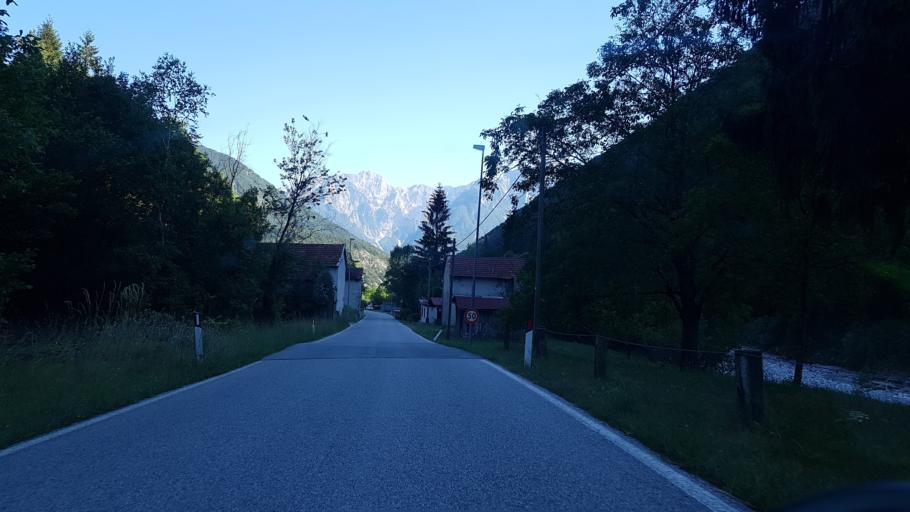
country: IT
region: Friuli Venezia Giulia
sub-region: Provincia di Udine
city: Moggio Udinese
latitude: 46.4341
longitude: 13.1989
